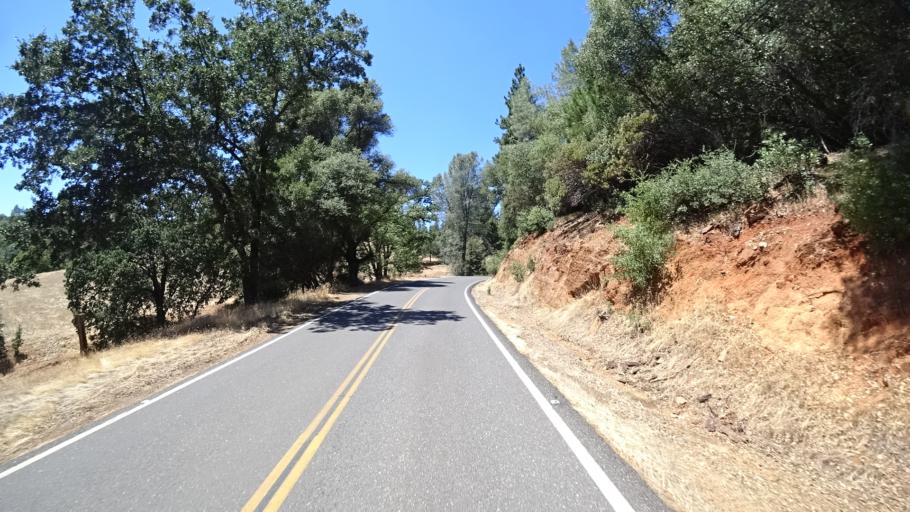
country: US
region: California
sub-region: Calaveras County
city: Murphys
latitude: 38.1383
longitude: -120.4735
